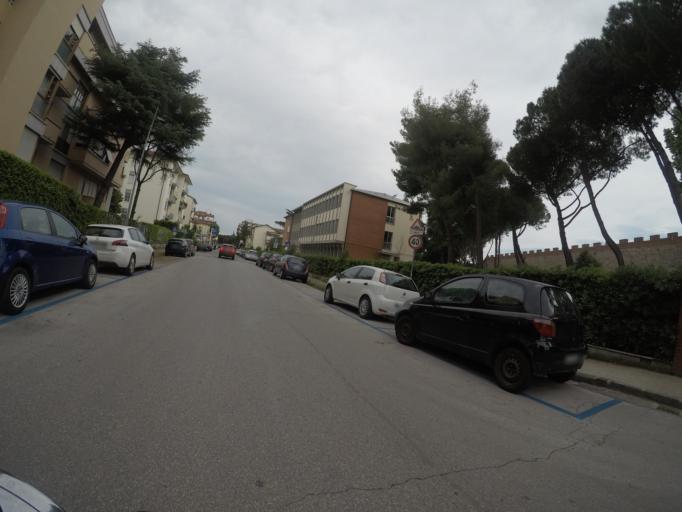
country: IT
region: Tuscany
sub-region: Province of Pisa
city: Pisa
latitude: 43.7218
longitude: 10.4094
